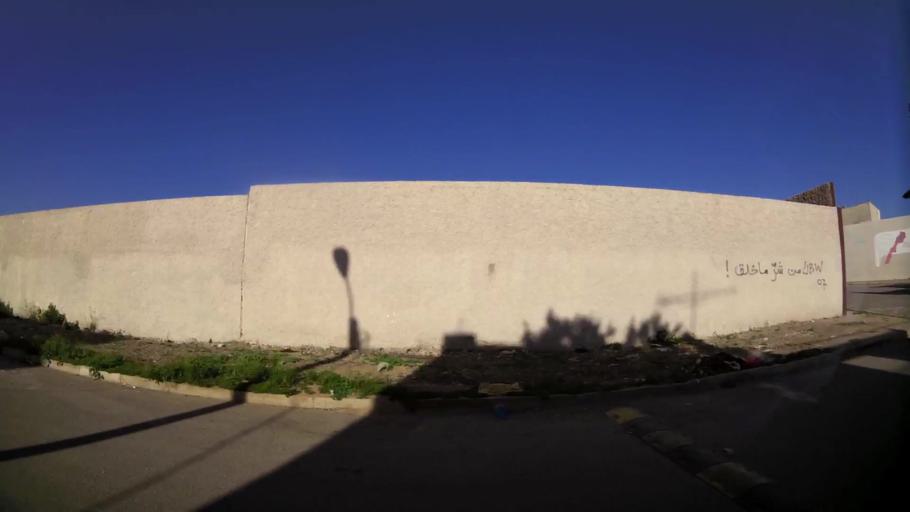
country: MA
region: Oriental
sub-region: Oujda-Angad
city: Oujda
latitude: 34.6961
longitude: -1.9167
